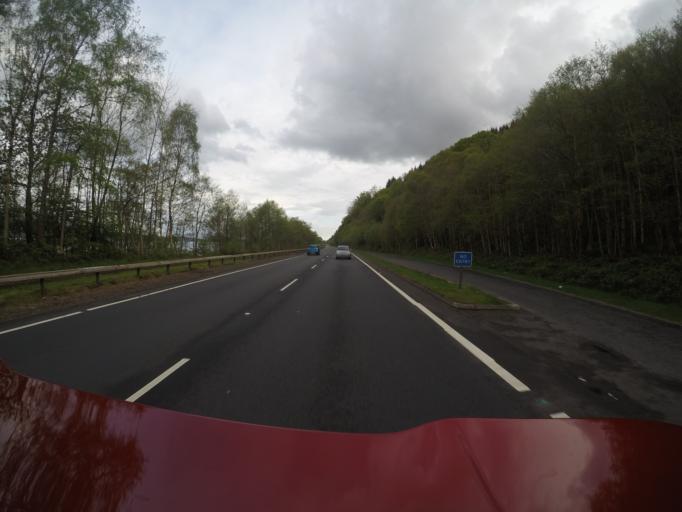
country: GB
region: Scotland
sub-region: Argyll and Bute
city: Helensburgh
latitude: 56.1364
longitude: -4.6591
